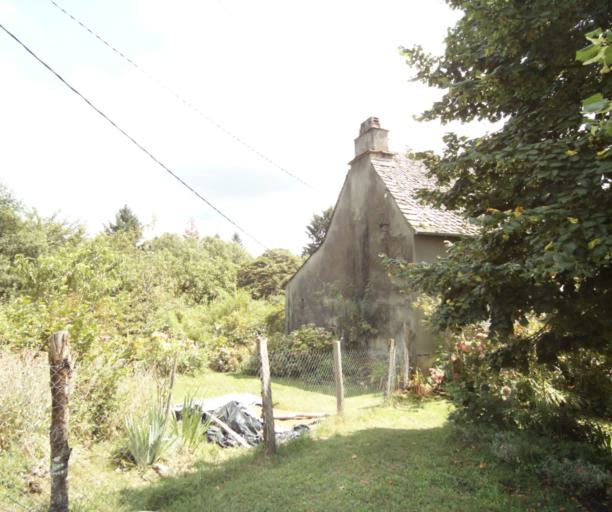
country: FR
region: Limousin
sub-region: Departement de la Correze
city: Sainte-Fortunade
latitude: 45.1964
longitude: 1.8425
